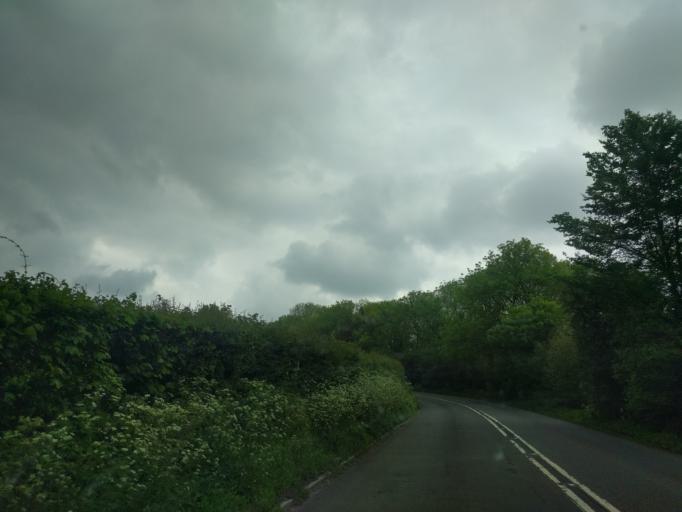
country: GB
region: England
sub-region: Somerset
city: Shepton Mallet
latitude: 51.1275
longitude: -2.5689
